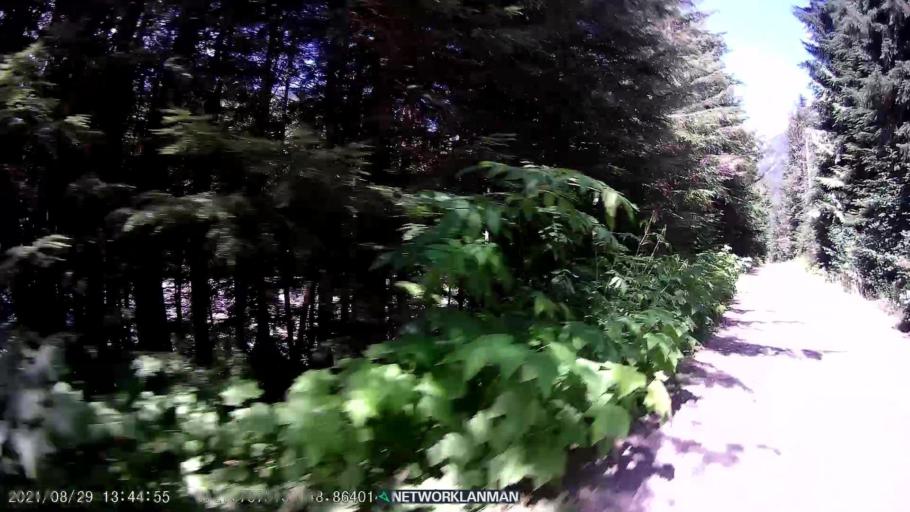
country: CA
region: British Columbia
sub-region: Fraser Valley Regional District
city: Chilliwack
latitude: 48.8641
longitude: -121.7675
